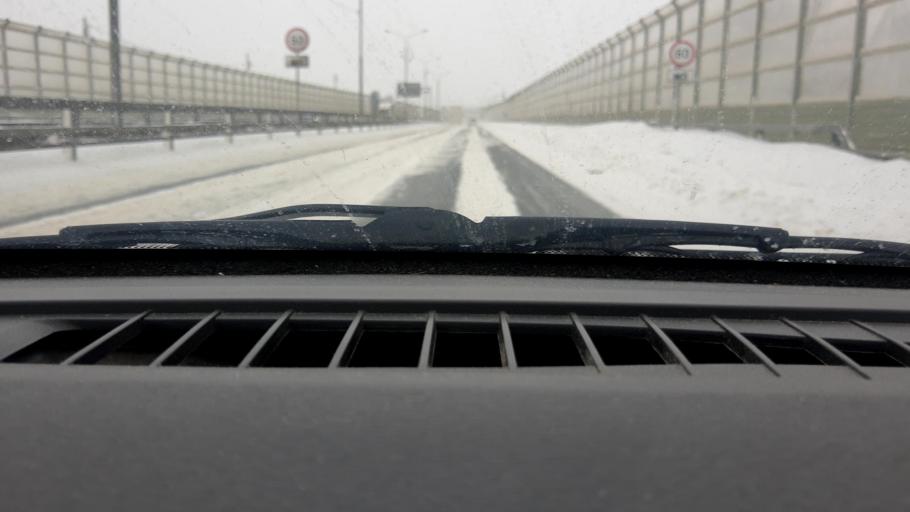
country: RU
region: Moskovskaya
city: Demikhovo
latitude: 55.8571
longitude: 38.8832
